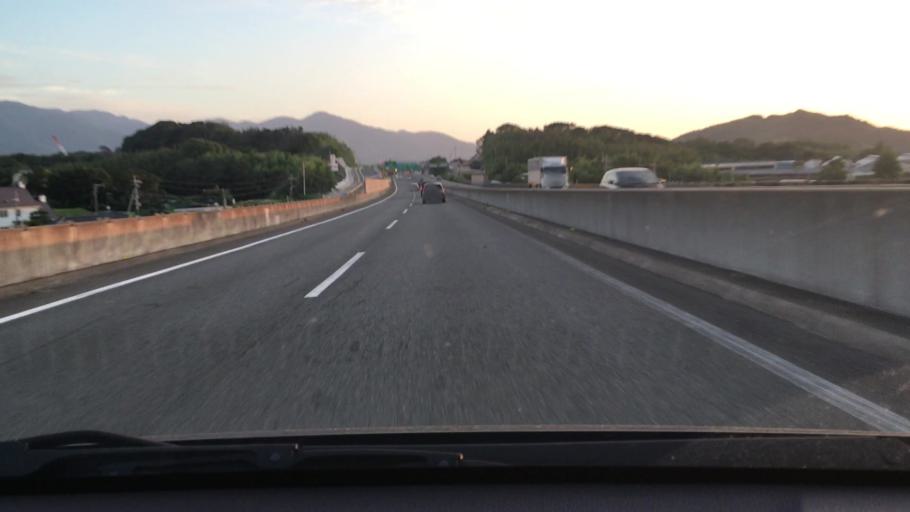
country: JP
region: Fukuoka
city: Maebaru-chuo
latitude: 33.5457
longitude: 130.2076
